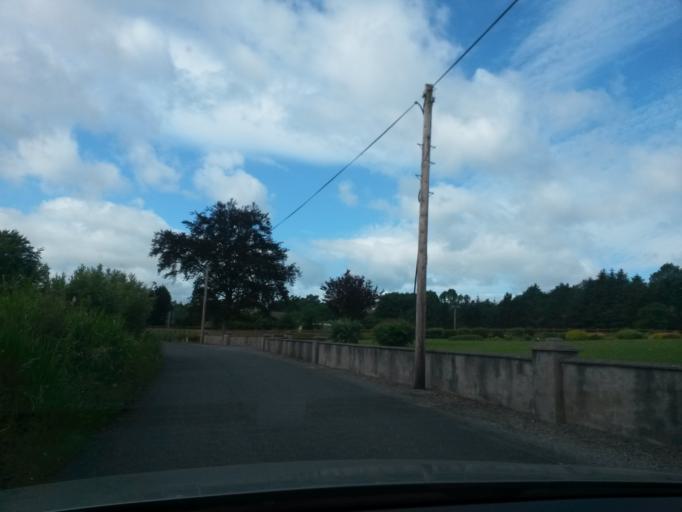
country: IE
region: Connaught
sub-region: Sligo
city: Sligo
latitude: 54.2396
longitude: -8.4462
